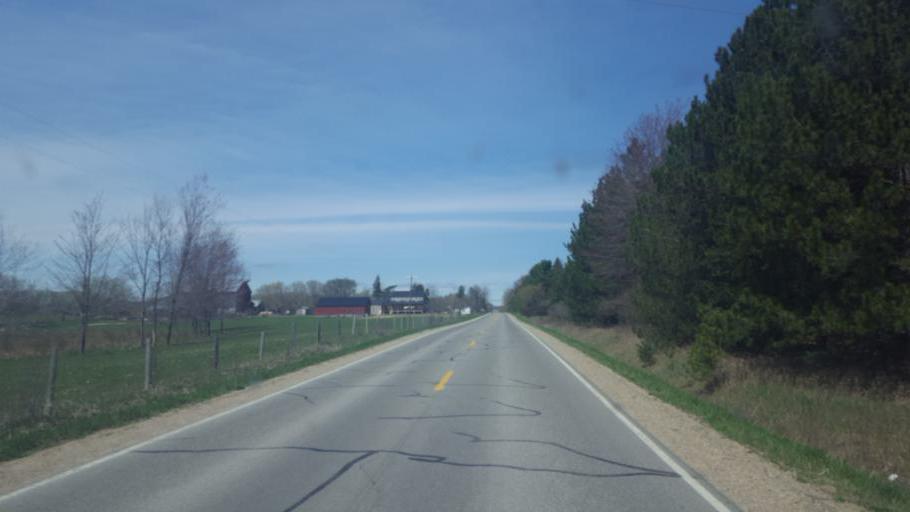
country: US
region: Michigan
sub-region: Gladwin County
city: Gladwin
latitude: 43.9381
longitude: -84.5853
